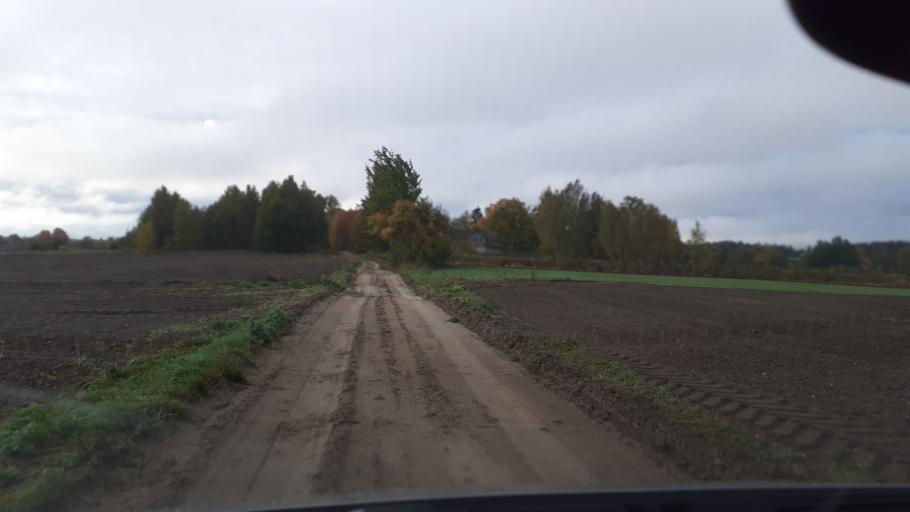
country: LV
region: Kuldigas Rajons
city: Kuldiga
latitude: 56.9752
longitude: 21.9394
